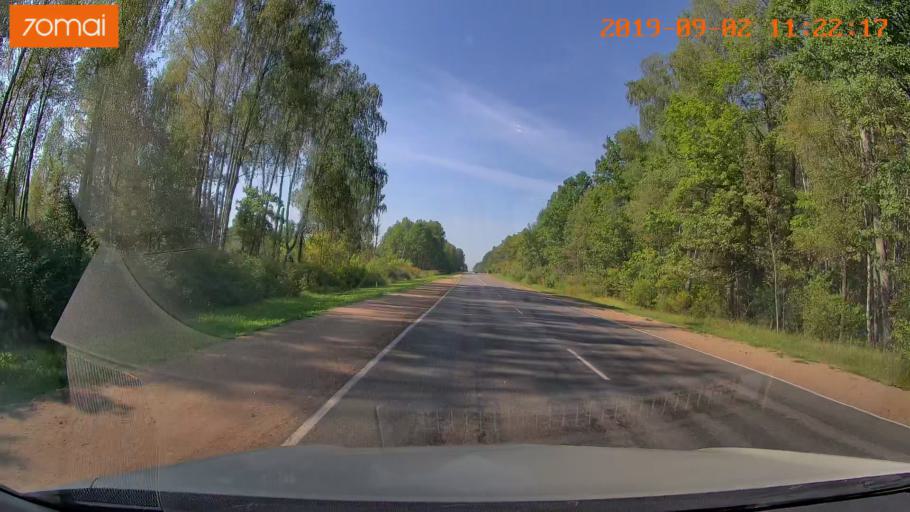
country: RU
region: Smolensk
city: Roslavl'
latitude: 54.0274
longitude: 33.0172
